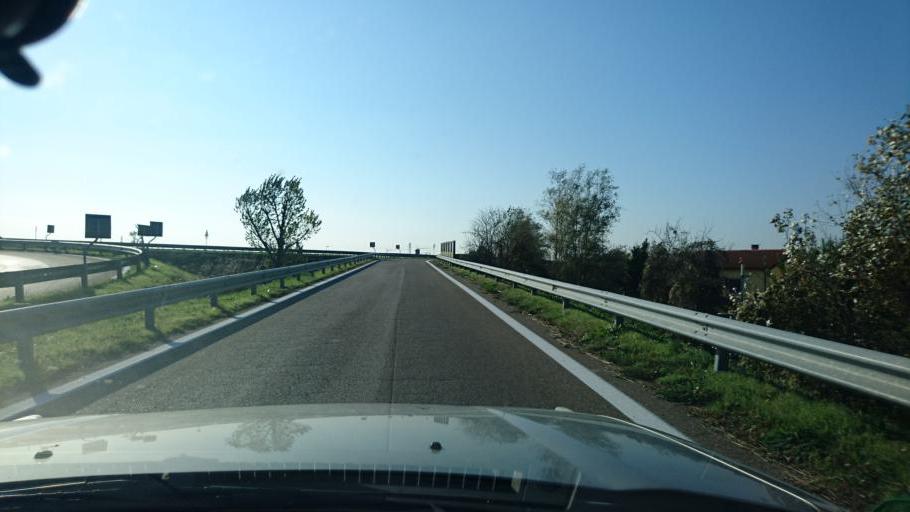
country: IT
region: Veneto
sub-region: Provincia di Padova
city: Monselice
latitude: 45.2099
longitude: 11.7564
